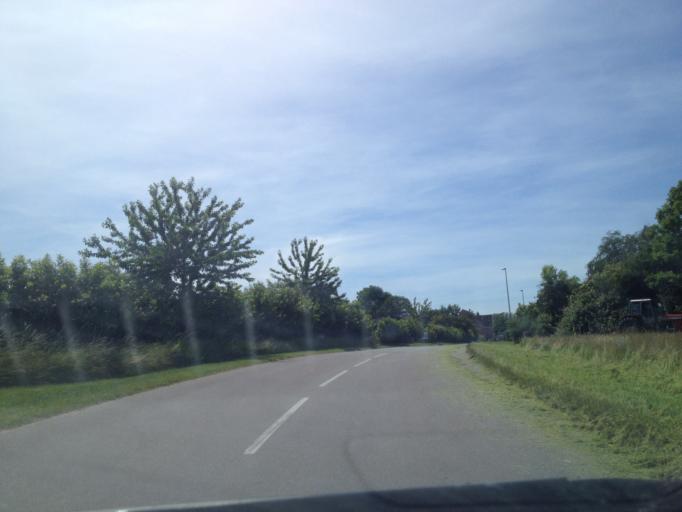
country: DK
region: Central Jutland
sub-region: Samso Kommune
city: Tranebjerg
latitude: 55.8346
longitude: 10.6011
